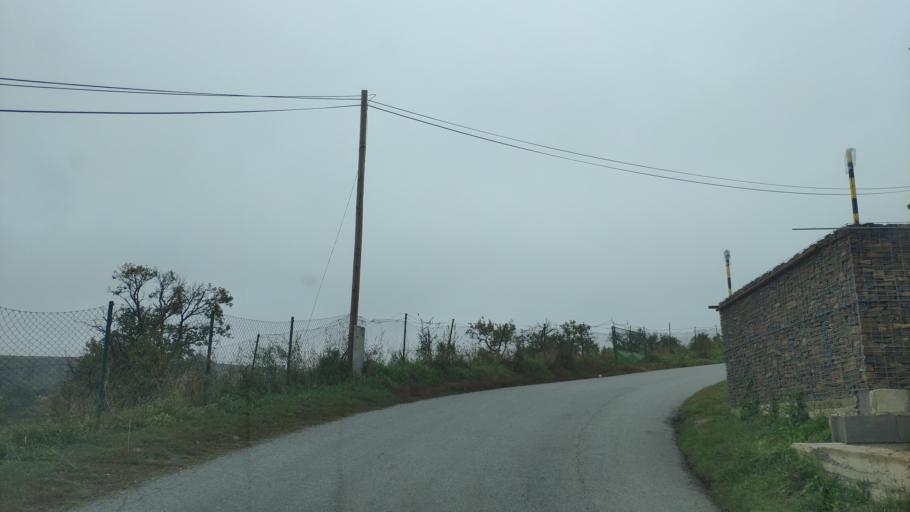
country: SK
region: Presovsky
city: Vranov nad Topl'ou
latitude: 48.8799
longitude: 21.4493
